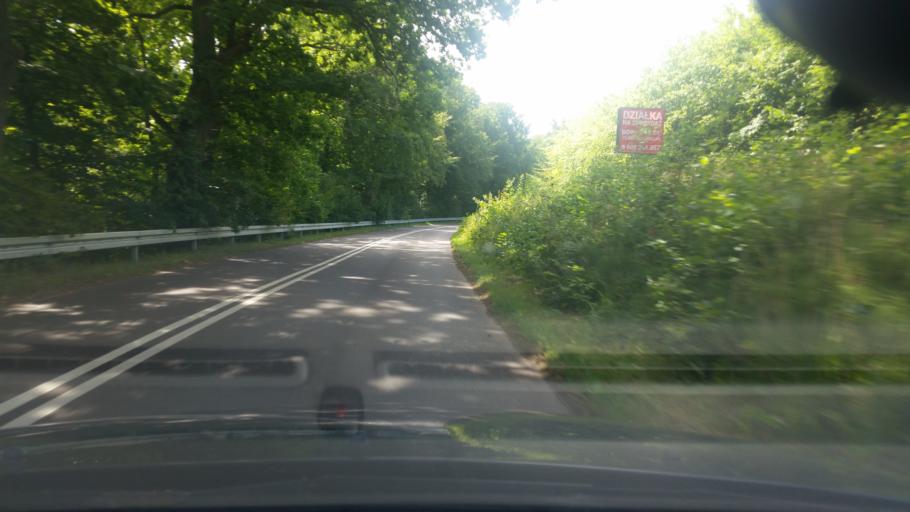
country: PL
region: Pomeranian Voivodeship
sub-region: Powiat wejherowski
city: Choczewo
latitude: 54.7576
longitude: 17.7516
